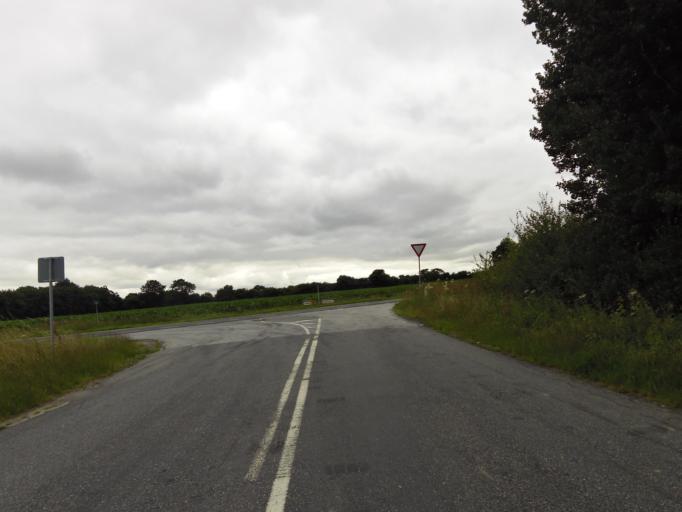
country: DK
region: South Denmark
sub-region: Haderslev Kommune
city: Gram
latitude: 55.3072
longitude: 9.1358
